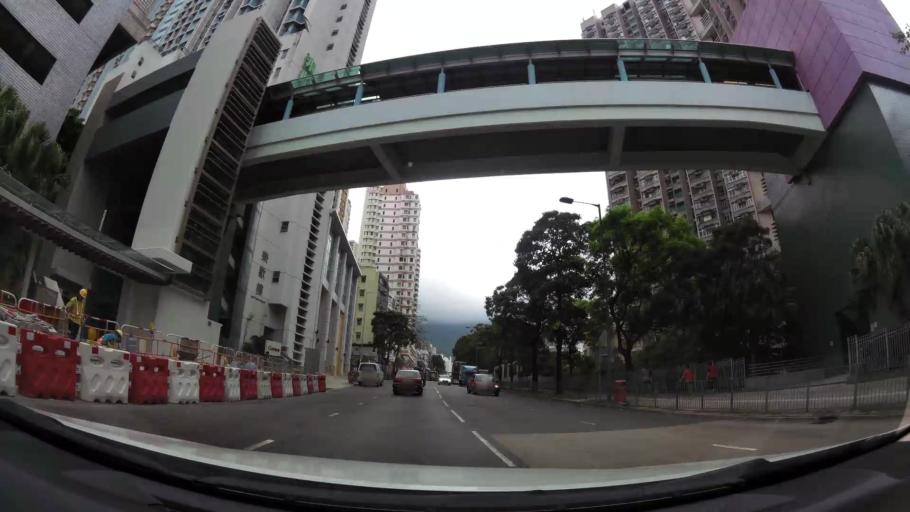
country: HK
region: Wong Tai Sin
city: Wong Tai Sin
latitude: 22.3459
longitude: 114.2002
